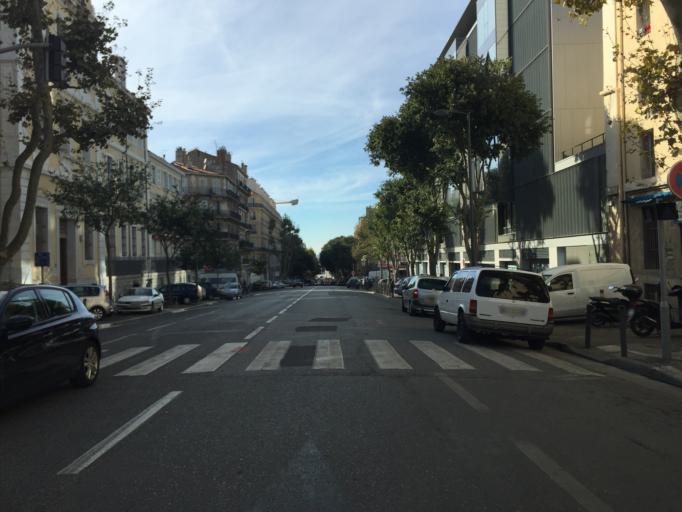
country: FR
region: Provence-Alpes-Cote d'Azur
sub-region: Departement des Bouches-du-Rhone
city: Marseille 03
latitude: 43.3019
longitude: 5.3724
